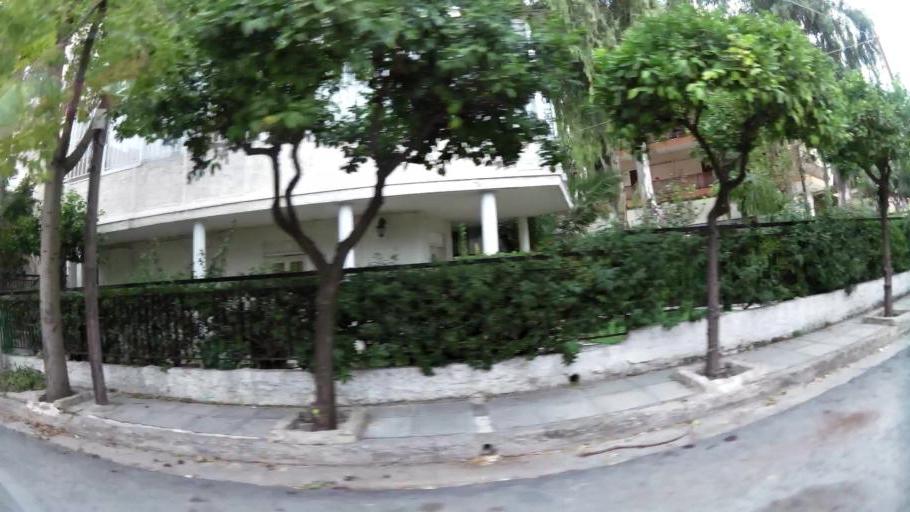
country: GR
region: Attica
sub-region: Nomarchia Athinas
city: Ilion
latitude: 38.0353
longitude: 23.7111
